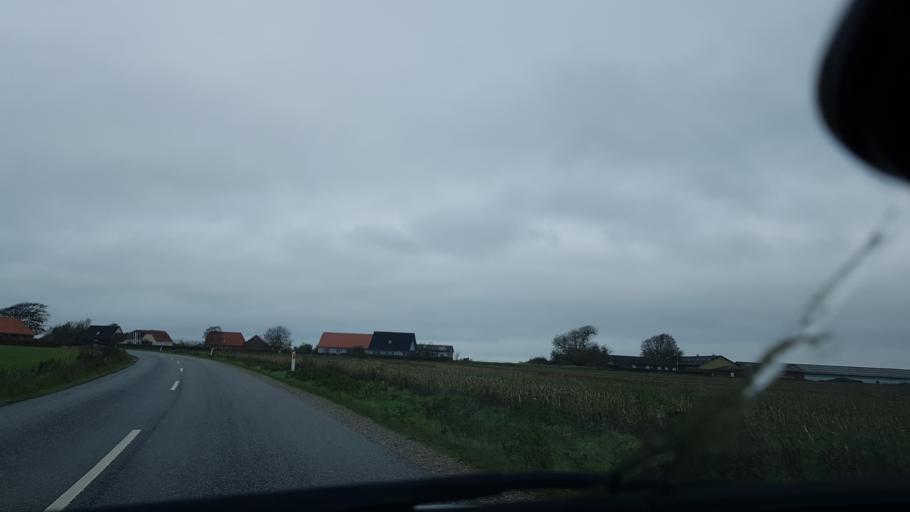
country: DK
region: South Denmark
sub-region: Tonder Kommune
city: Sherrebek
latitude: 55.2371
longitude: 8.8343
